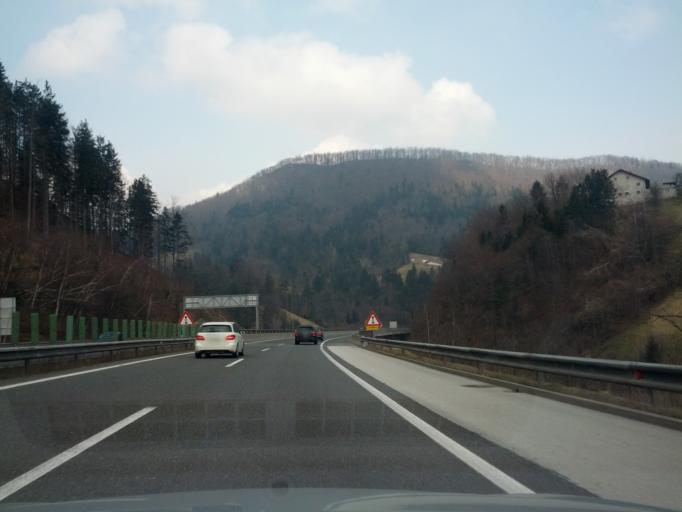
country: SI
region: Vransko
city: Vransko
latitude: 46.2019
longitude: 14.9002
